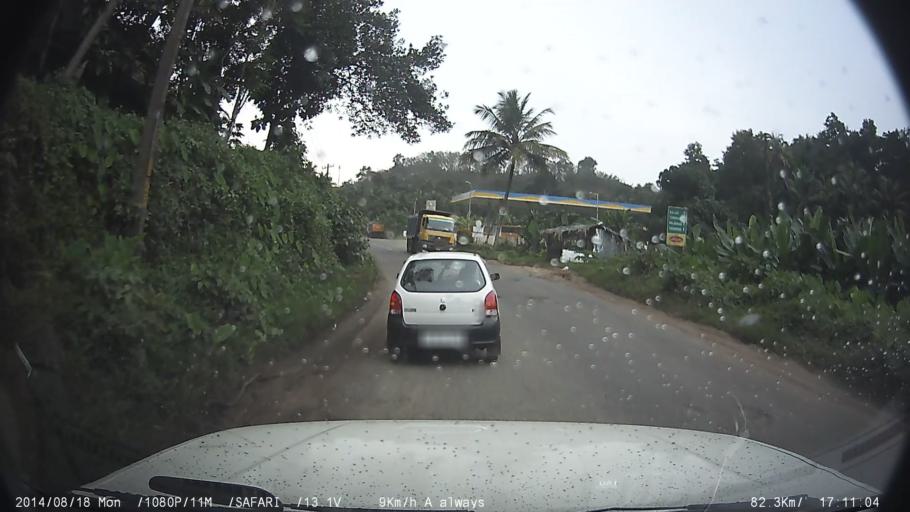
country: IN
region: Kerala
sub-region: Ernakulam
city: Piravam
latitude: 9.8761
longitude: 76.5961
